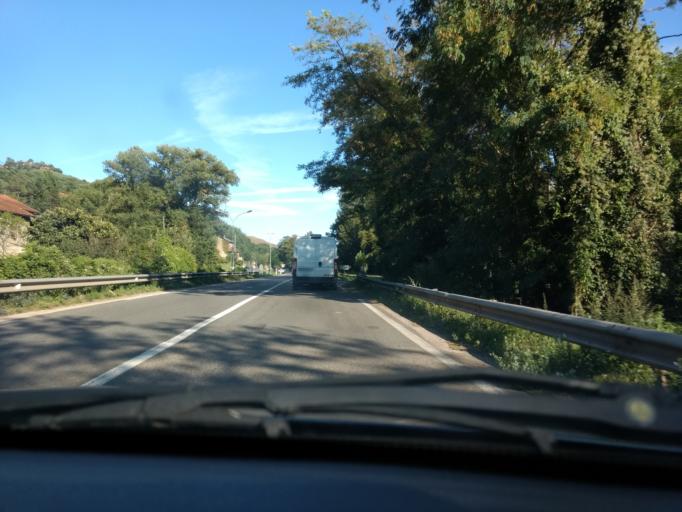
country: FR
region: Midi-Pyrenees
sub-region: Departement de l'Aveyron
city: Decazeville
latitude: 44.5563
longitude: 2.2797
